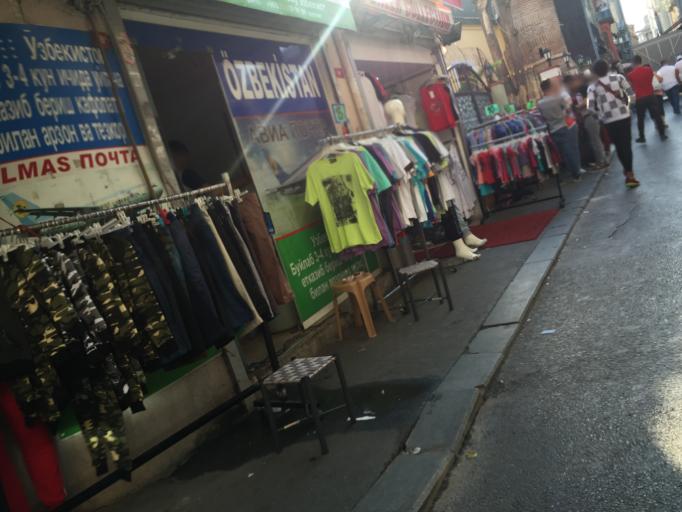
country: TR
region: Istanbul
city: Istanbul
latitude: 41.0058
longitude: 28.9568
